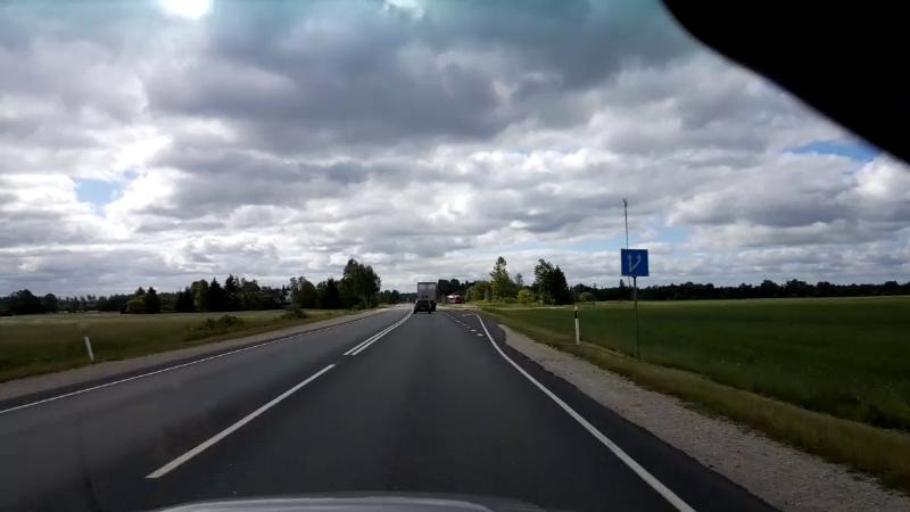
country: EE
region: Raplamaa
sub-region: Maerjamaa vald
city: Marjamaa
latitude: 58.7708
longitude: 24.4161
